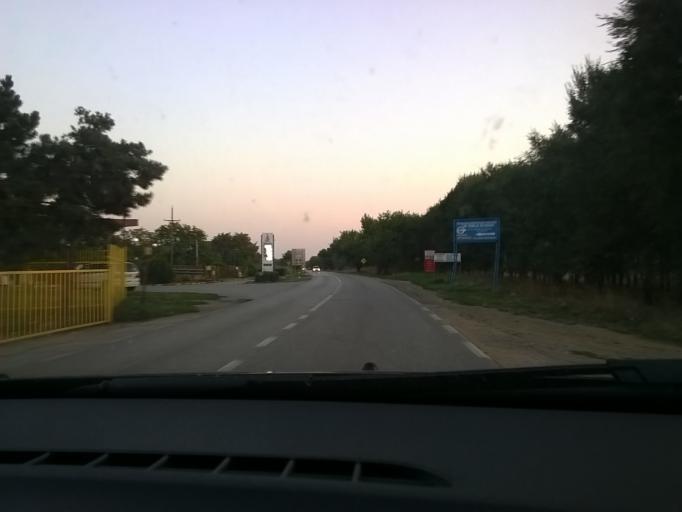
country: RS
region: Autonomna Pokrajina Vojvodina
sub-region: Juznobanatski Okrug
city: Vrsac
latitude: 45.1032
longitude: 21.2982
